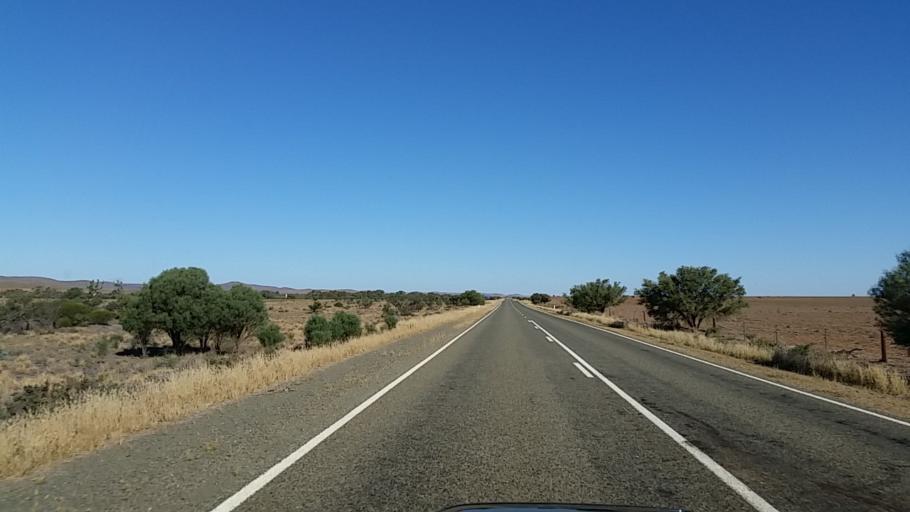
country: AU
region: South Australia
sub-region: Flinders Ranges
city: Quorn
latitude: -32.4040
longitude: 138.5166
